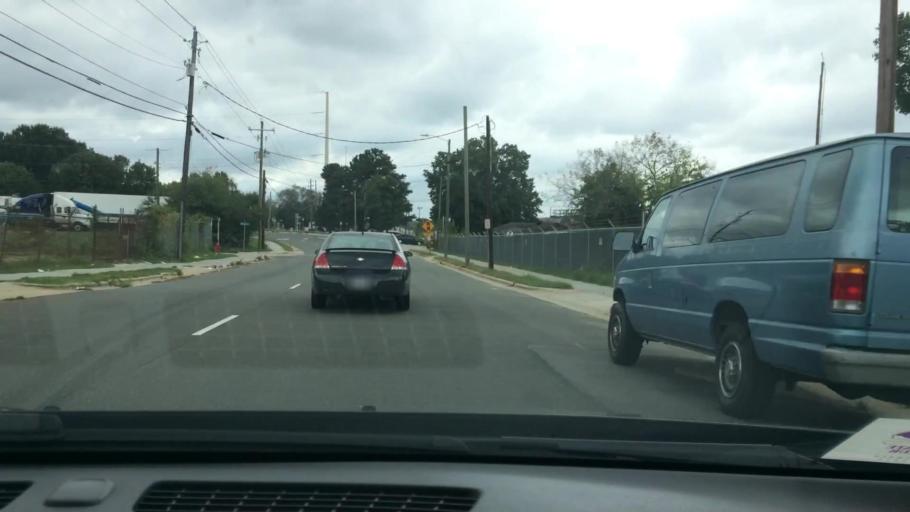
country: US
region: North Carolina
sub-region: Wake County
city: Raleigh
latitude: 35.7653
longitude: -78.6373
